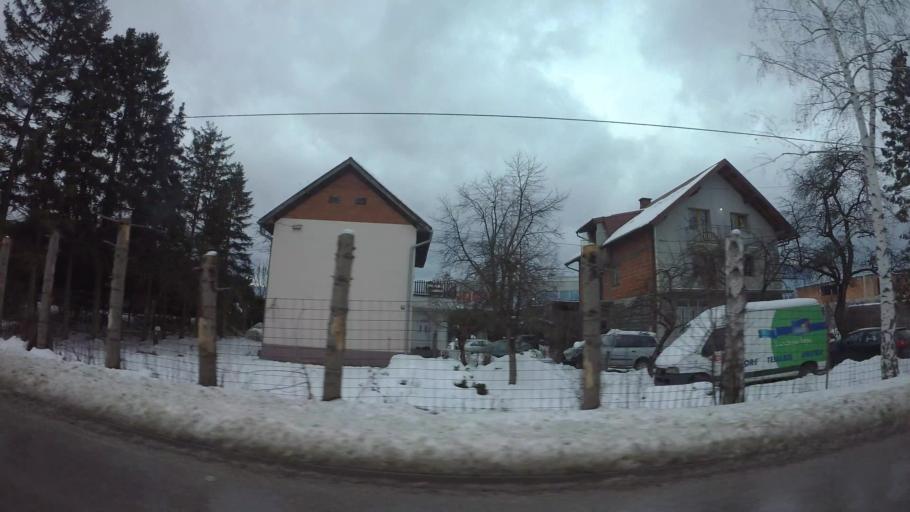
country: BA
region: Federation of Bosnia and Herzegovina
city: Vogosca
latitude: 43.8799
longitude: 18.3066
